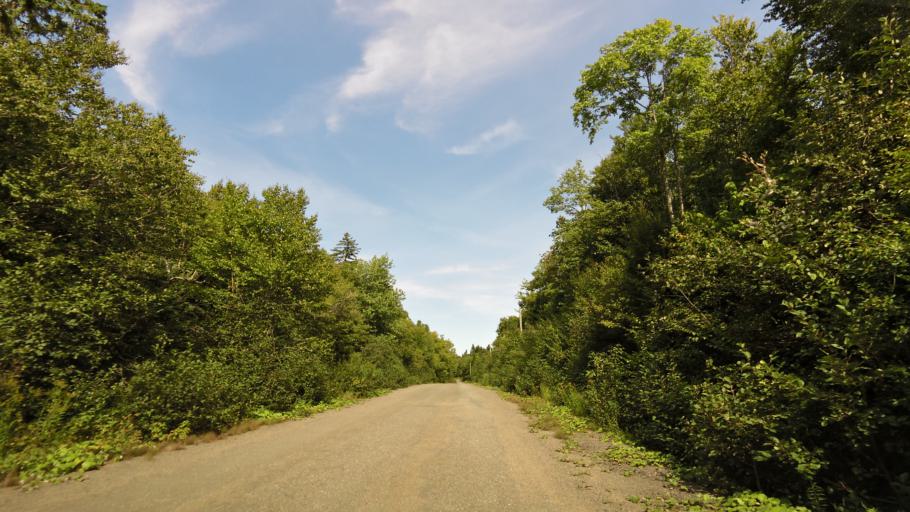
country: CA
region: New Brunswick
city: Hampton
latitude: 45.5681
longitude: -65.8362
